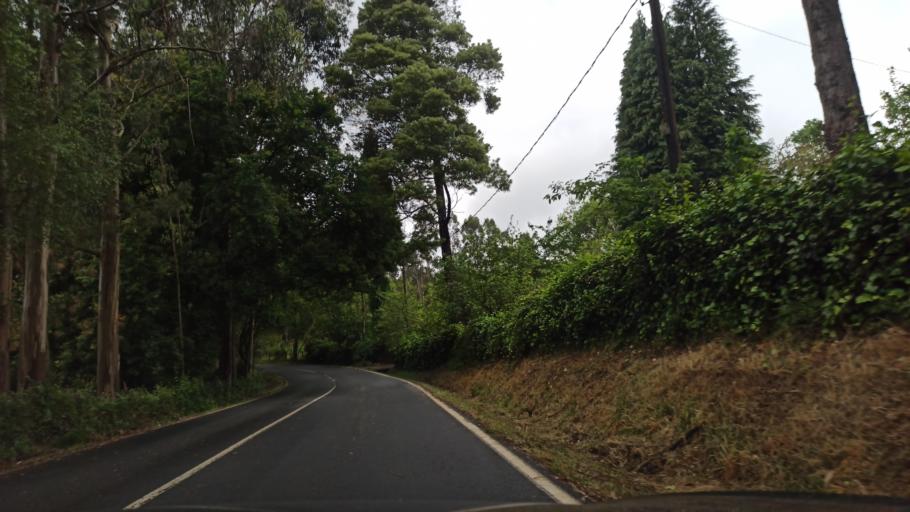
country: ES
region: Galicia
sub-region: Provincia da Coruna
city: Santiso
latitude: 42.7846
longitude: -8.0531
